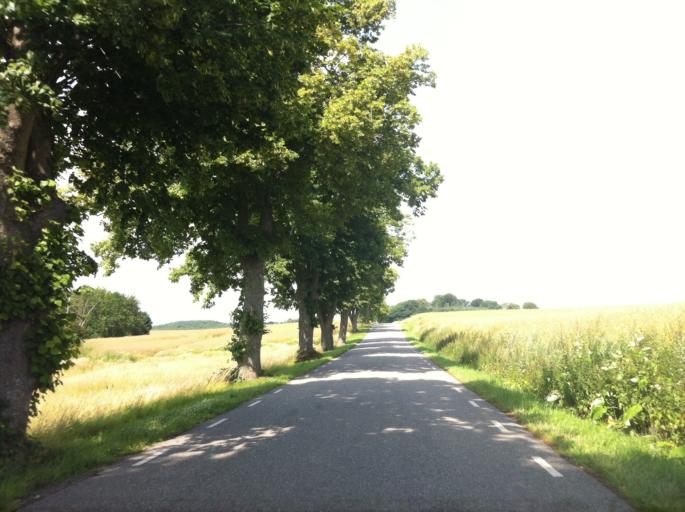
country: SE
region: Skane
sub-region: Trelleborgs Kommun
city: Anderslov
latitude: 55.4514
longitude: 13.4020
